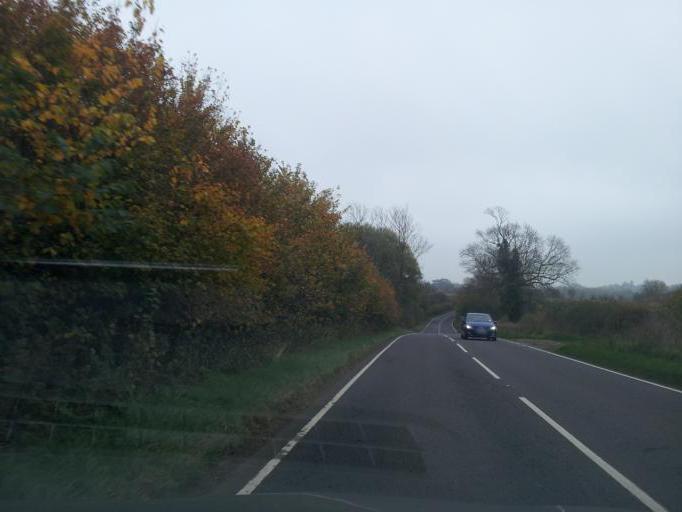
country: GB
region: England
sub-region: Buckinghamshire
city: Buckingham
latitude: 52.0044
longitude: -1.0069
